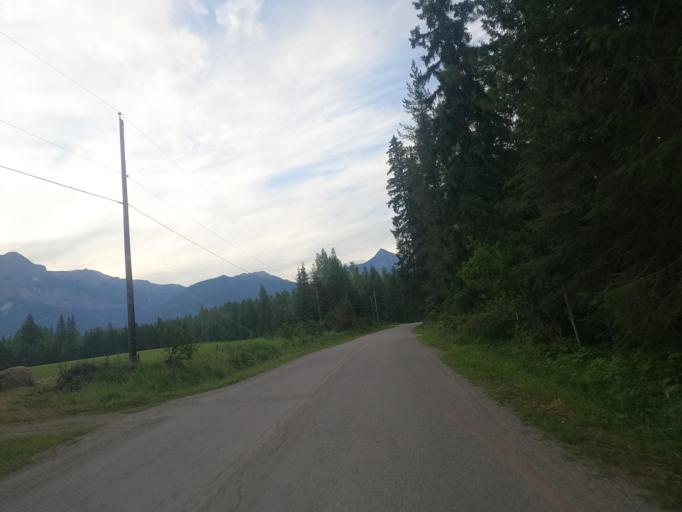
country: CA
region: British Columbia
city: Golden
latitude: 51.4320
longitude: -117.0480
